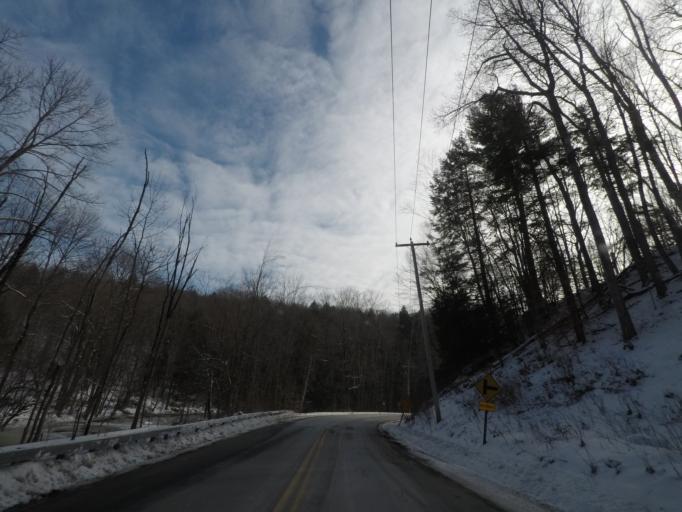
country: US
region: New York
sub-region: Rensselaer County
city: Averill Park
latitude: 42.5571
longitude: -73.5065
